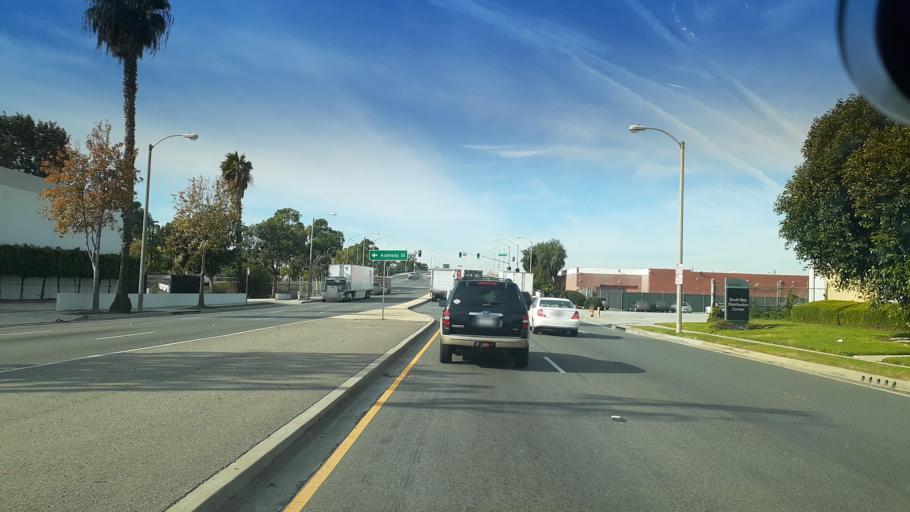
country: US
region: California
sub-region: Los Angeles County
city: Compton
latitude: 33.8467
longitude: -118.2162
